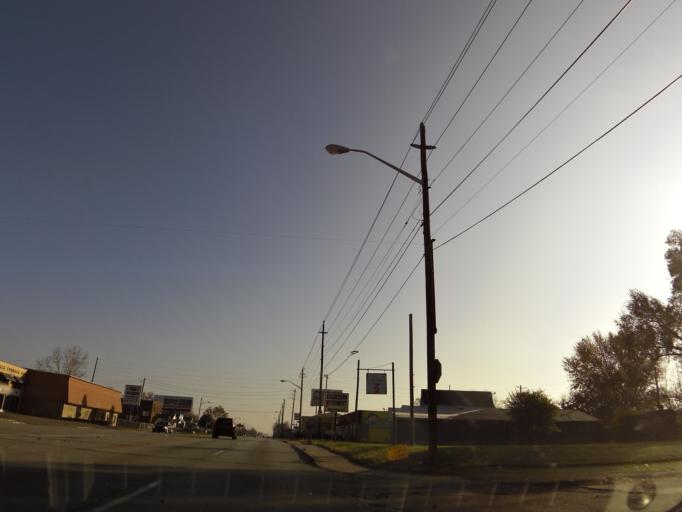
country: US
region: Indiana
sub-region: Marion County
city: Speedway
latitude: 39.7876
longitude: -86.2239
